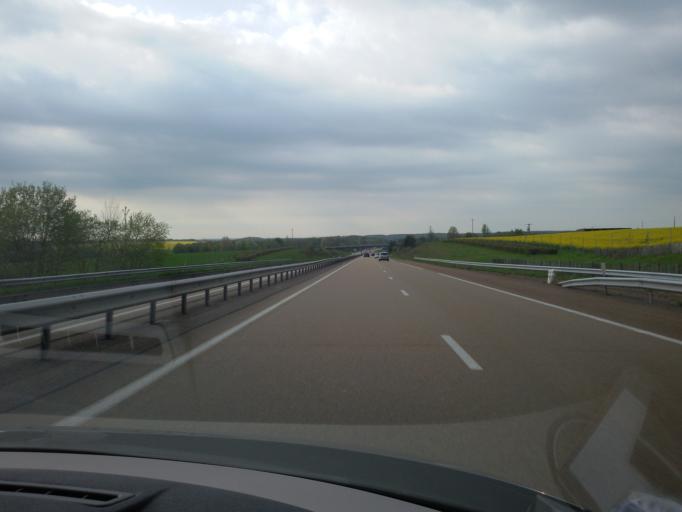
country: FR
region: Champagne-Ardenne
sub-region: Departement de la Haute-Marne
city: Chamarandes-Choignes
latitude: 47.9752
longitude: 5.1376
